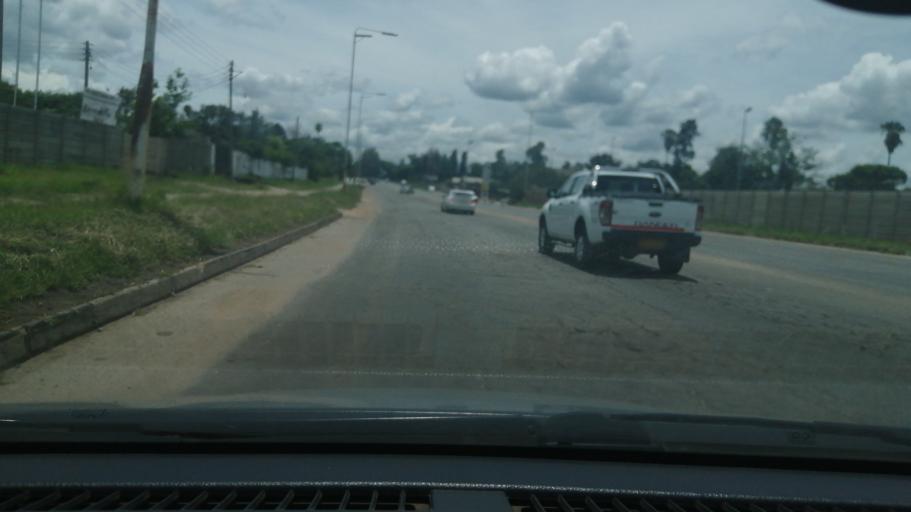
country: ZW
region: Harare
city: Harare
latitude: -17.8730
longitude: 31.0648
